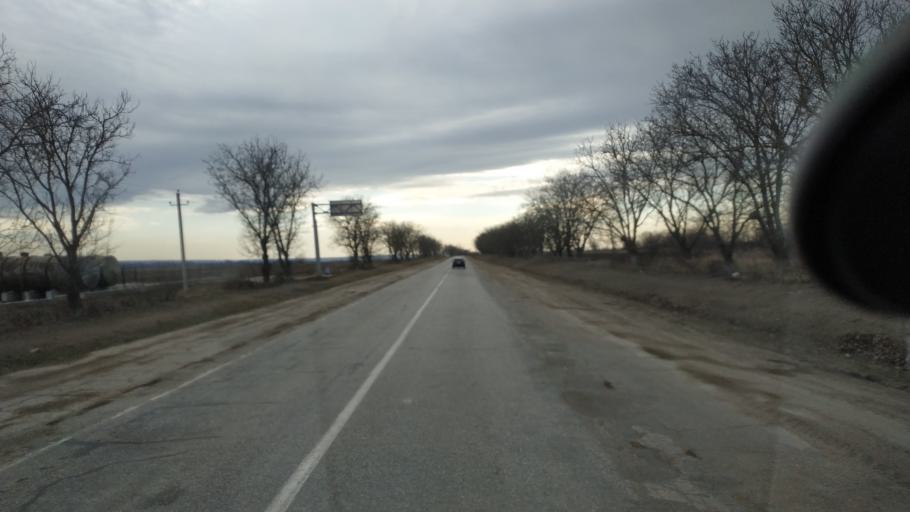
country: MD
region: Criuleni
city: Criuleni
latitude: 47.1988
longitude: 29.1524
